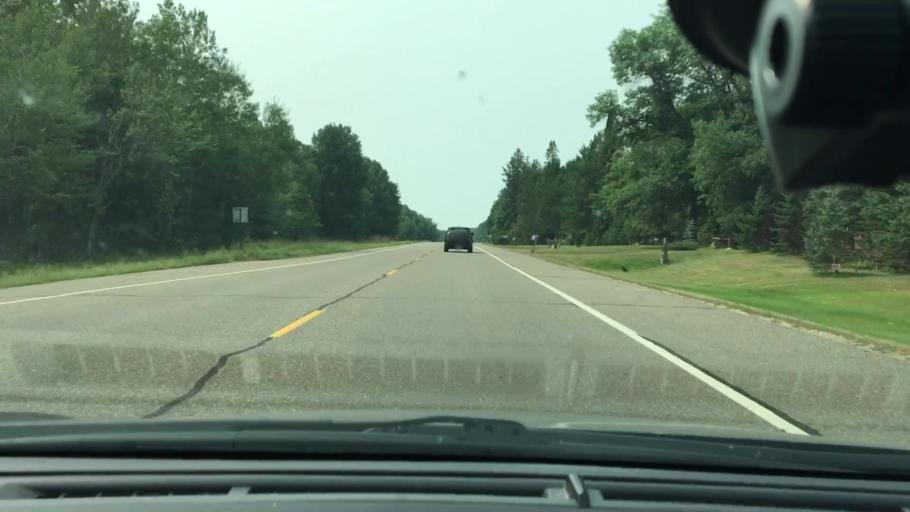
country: US
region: Minnesota
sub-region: Crow Wing County
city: Breezy Point
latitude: 46.5056
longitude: -94.1390
